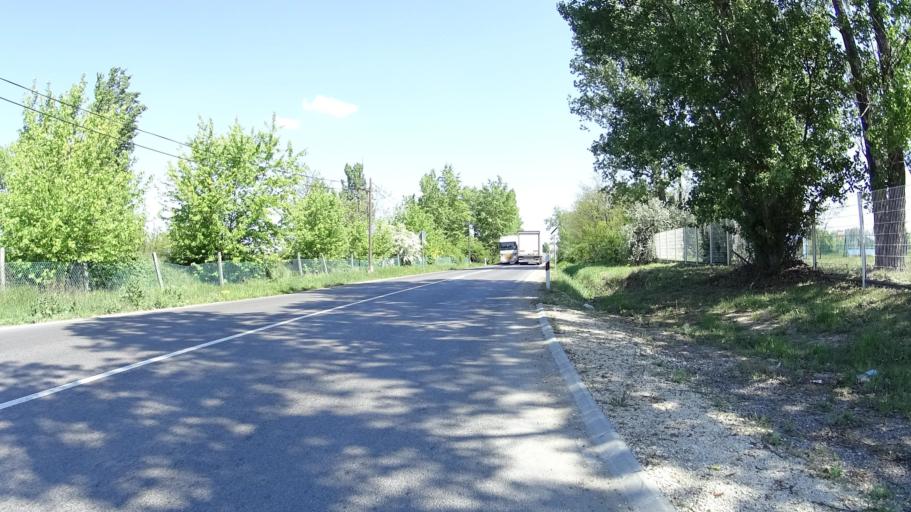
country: HU
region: Pest
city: Gyal
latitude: 47.3606
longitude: 19.2026
